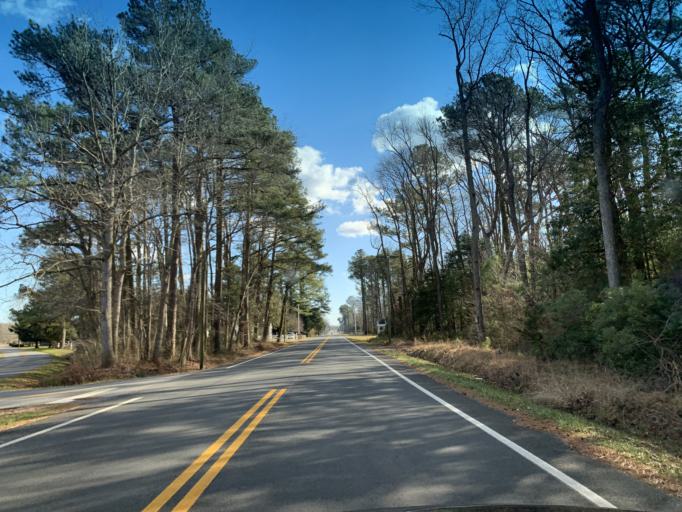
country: US
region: Maryland
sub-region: Worcester County
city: Berlin
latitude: 38.3606
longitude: -75.1997
